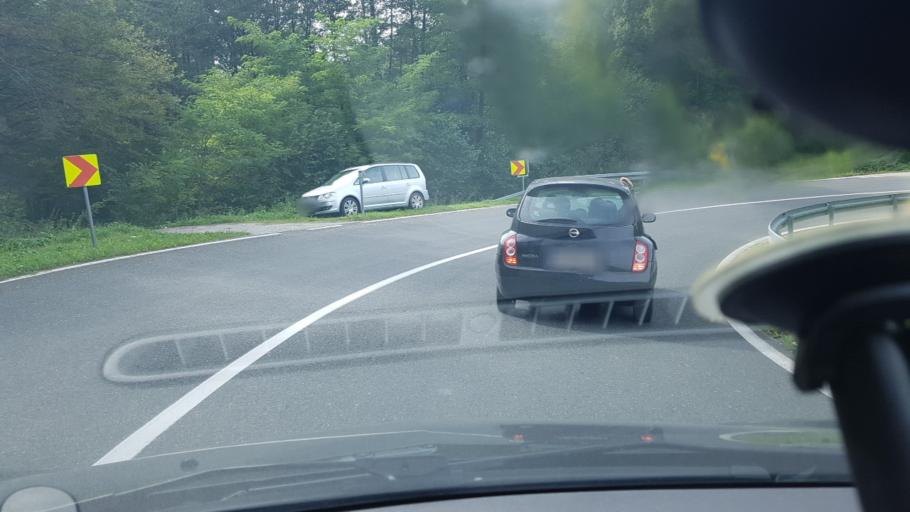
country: HR
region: Varazdinska
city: Ljubescica
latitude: 46.1403
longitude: 16.3597
